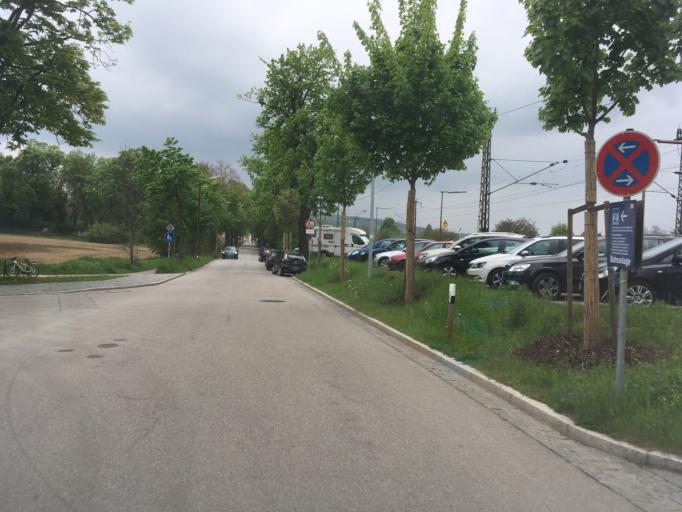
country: DE
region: Bavaria
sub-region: Upper Palatinate
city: Sinzing
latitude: 49.0114
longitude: 12.0485
